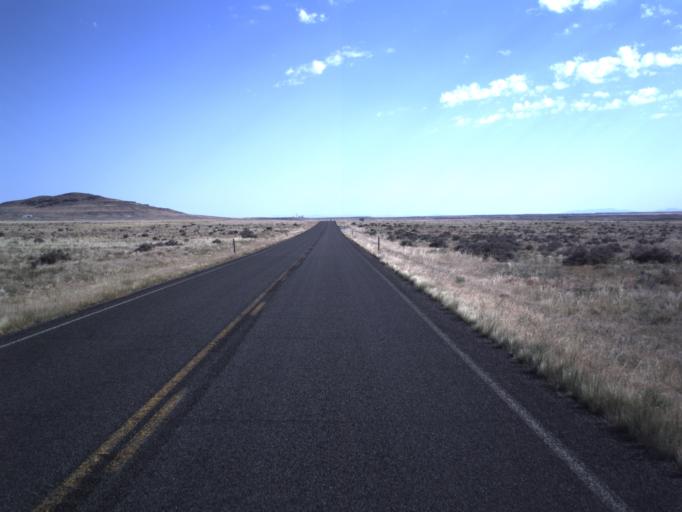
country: US
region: Utah
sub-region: Beaver County
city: Milford
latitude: 38.8443
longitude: -112.8443
